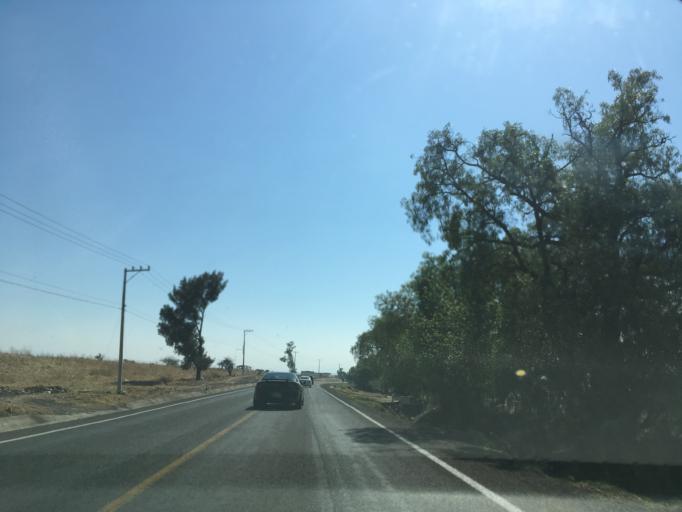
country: MX
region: Michoacan
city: Indaparapeo
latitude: 19.7922
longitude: -100.9582
